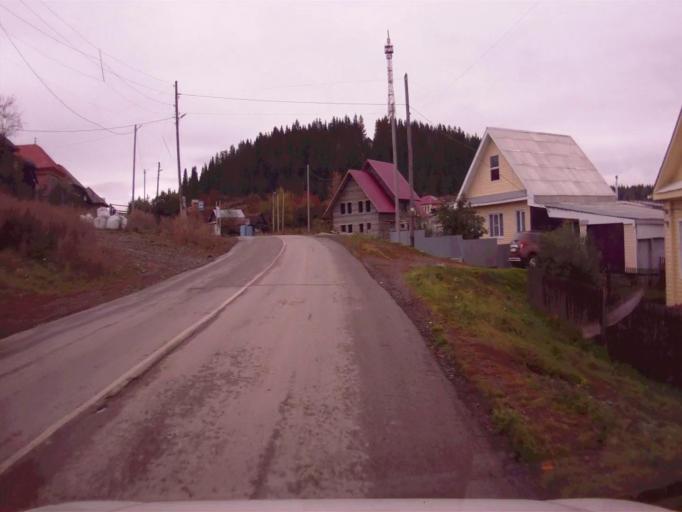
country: RU
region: Chelyabinsk
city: Nyazepetrovsk
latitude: 56.0611
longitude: 59.6146
